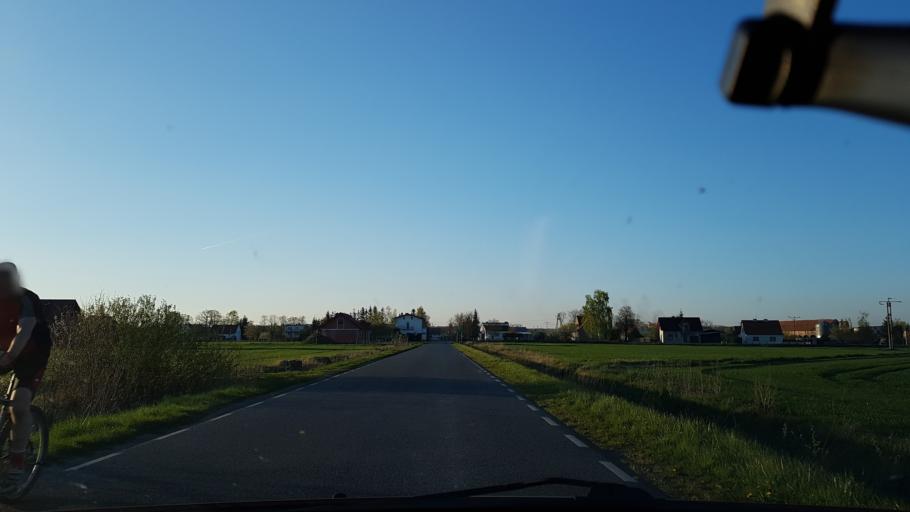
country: PL
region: Opole Voivodeship
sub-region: Powiat nyski
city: Otmuchow
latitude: 50.4437
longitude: 17.1701
